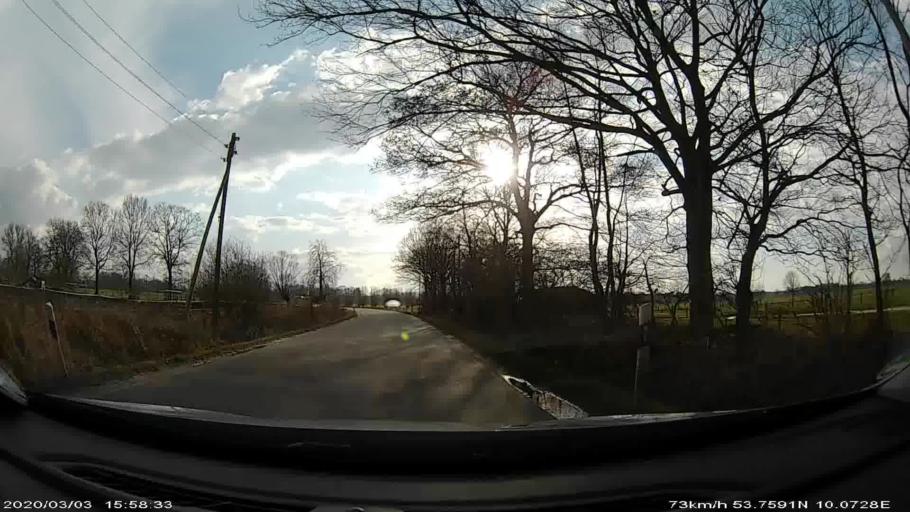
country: DE
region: Schleswig-Holstein
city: Tangstedt
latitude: 53.7602
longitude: 10.0739
